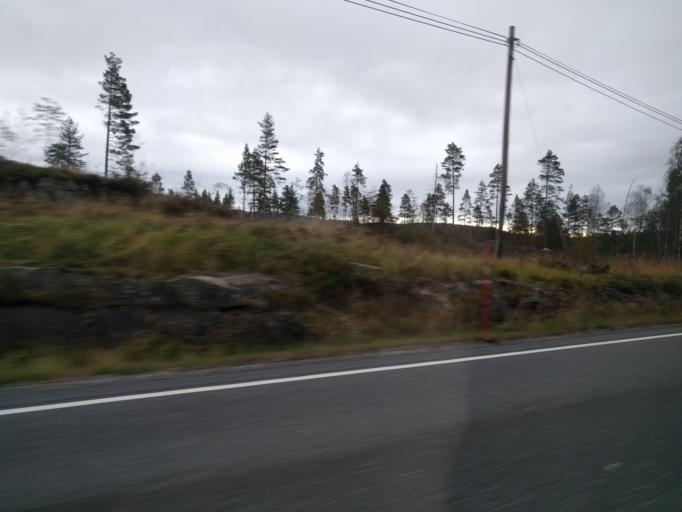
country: NO
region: Aust-Agder
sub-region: Evje og Hornnes
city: Evje
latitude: 58.5153
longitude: 7.7686
